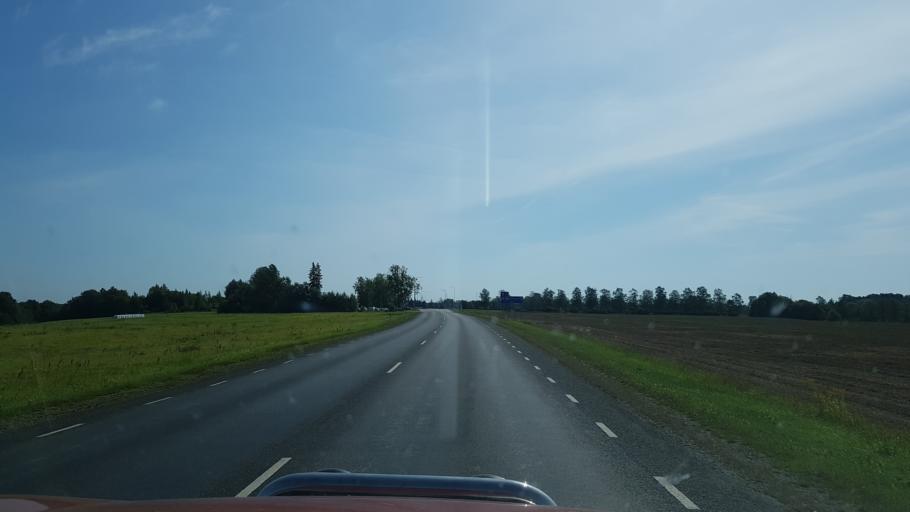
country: EE
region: Viljandimaa
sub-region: Viljandi linn
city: Viljandi
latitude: 58.3939
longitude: 25.5928
